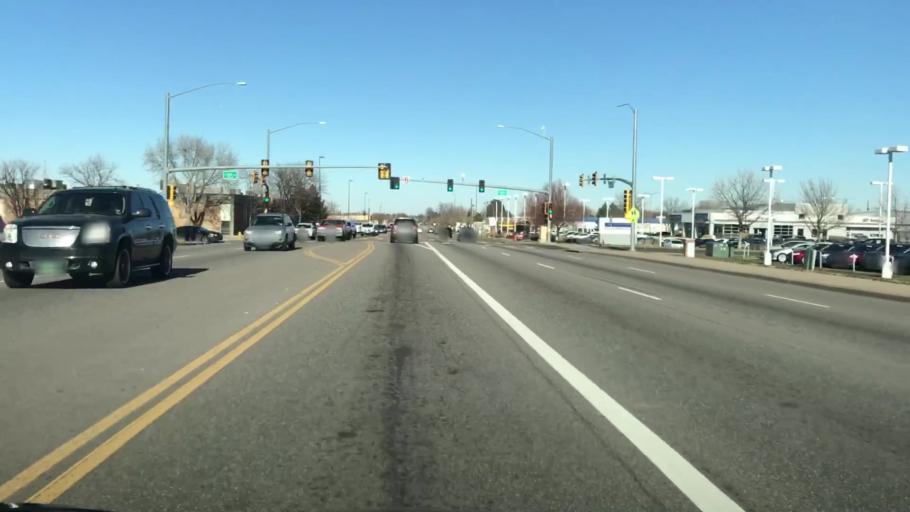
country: US
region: Colorado
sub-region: Adams County
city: Aurora
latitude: 39.7176
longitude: -104.8660
